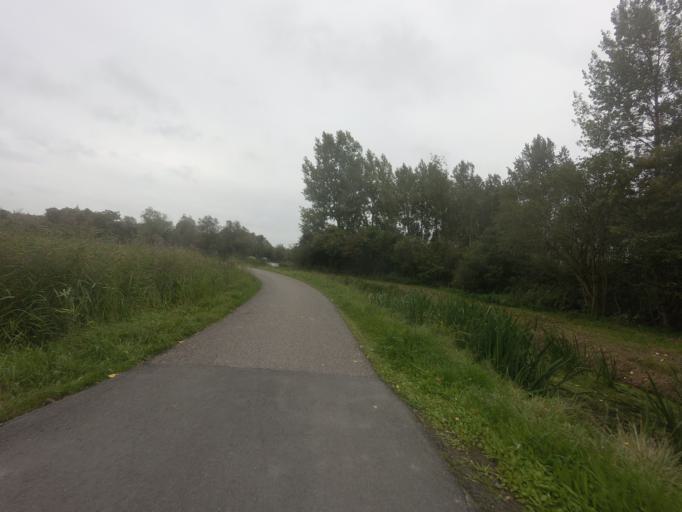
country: NL
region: Friesland
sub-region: Gemeente Leeuwarden
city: Bilgaard
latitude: 53.2205
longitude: 5.7897
